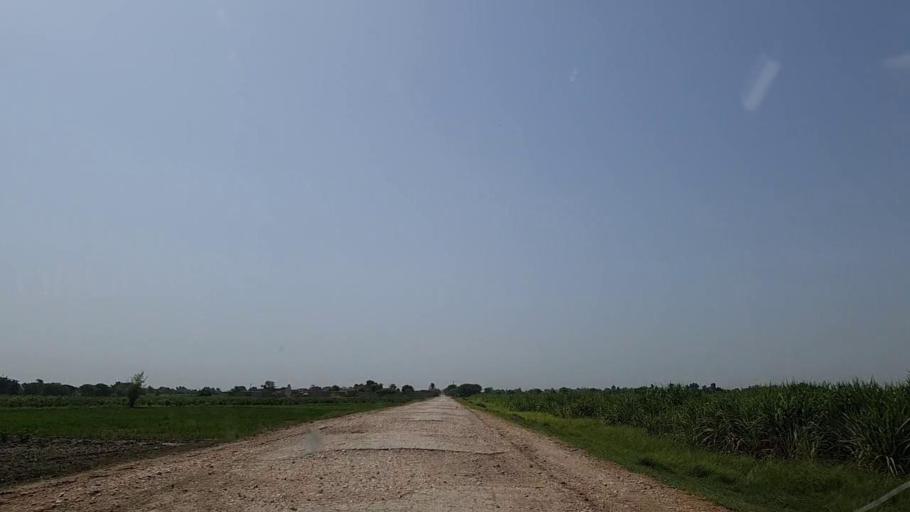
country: PK
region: Sindh
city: Naushahro Firoz
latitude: 26.8531
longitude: 68.0088
